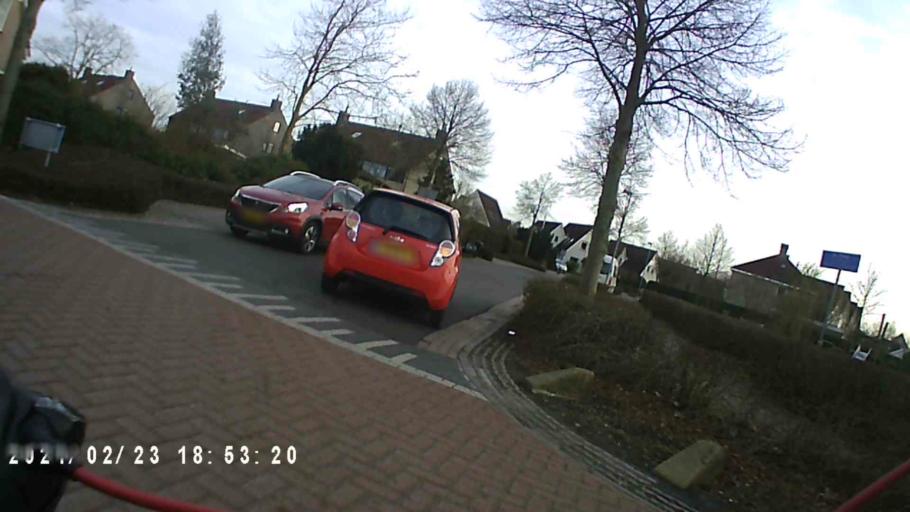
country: NL
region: Groningen
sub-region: Gemeente Winsum
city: Winsum
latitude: 53.3348
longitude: 6.5265
